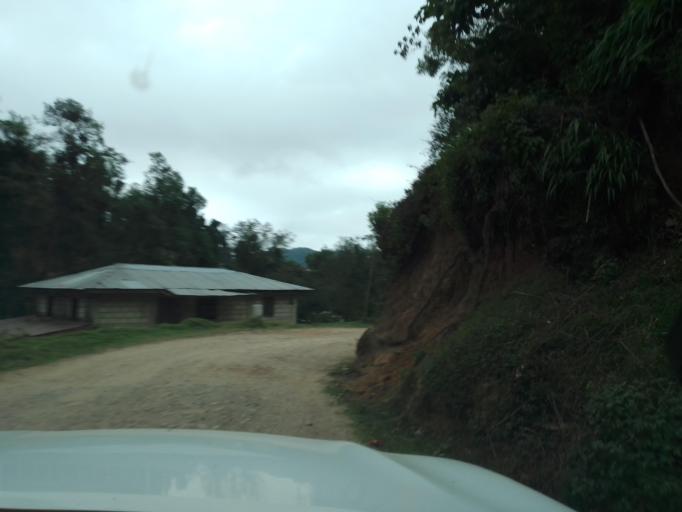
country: MX
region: Chiapas
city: Motozintla de Mendoza
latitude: 15.2184
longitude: -92.2323
